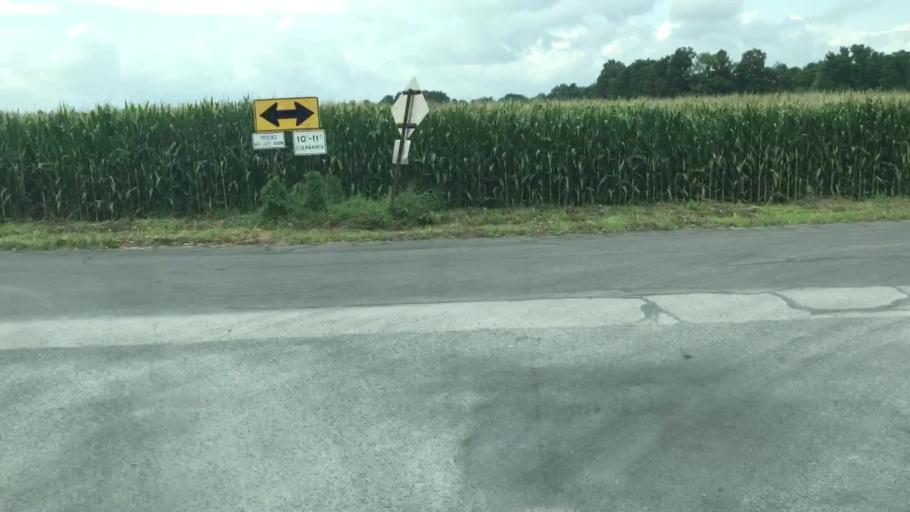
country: US
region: New York
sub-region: Cayuga County
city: Auburn
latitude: 42.9847
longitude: -76.5106
